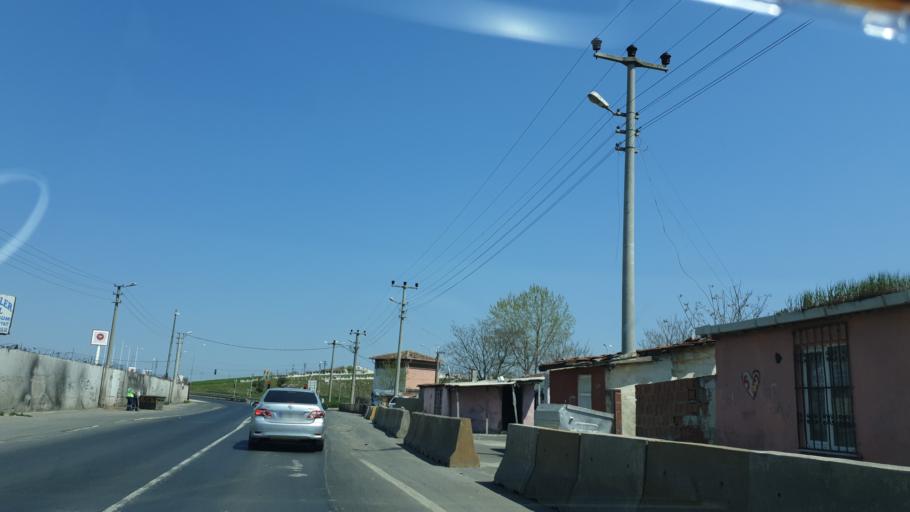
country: TR
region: Tekirdag
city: Corlu
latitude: 41.1704
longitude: 27.7990
